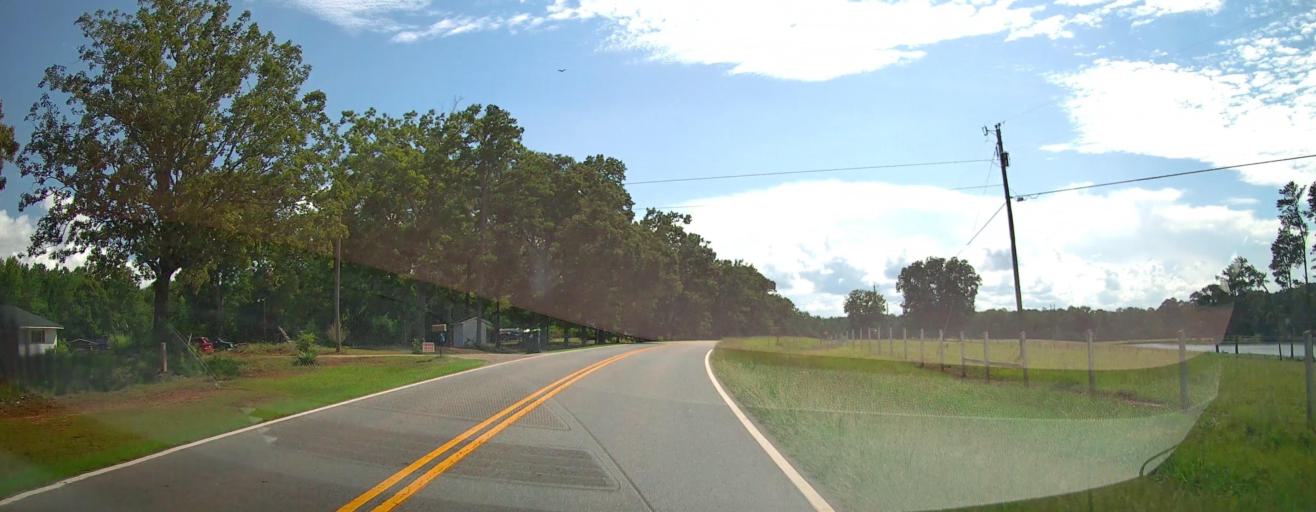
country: US
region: Georgia
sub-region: Upson County
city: Hannahs Mill
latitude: 32.9490
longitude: -84.3225
